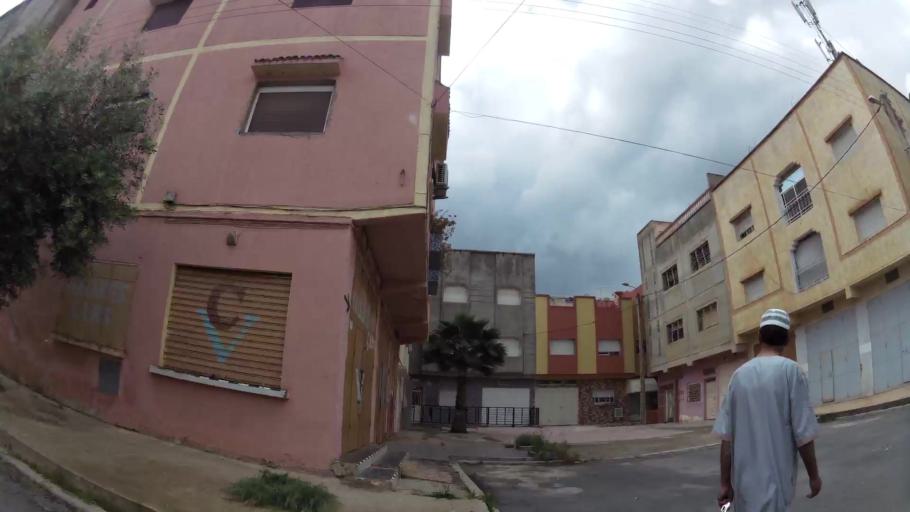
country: MA
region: Rabat-Sale-Zemmour-Zaer
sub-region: Khemisset
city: Tiflet
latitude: 33.8931
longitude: -6.3299
